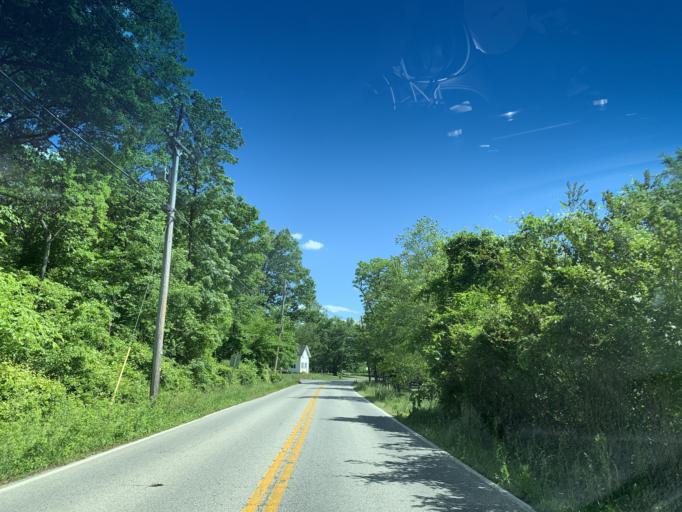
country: US
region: Maryland
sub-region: Cecil County
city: Elkton
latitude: 39.5951
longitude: -75.8643
